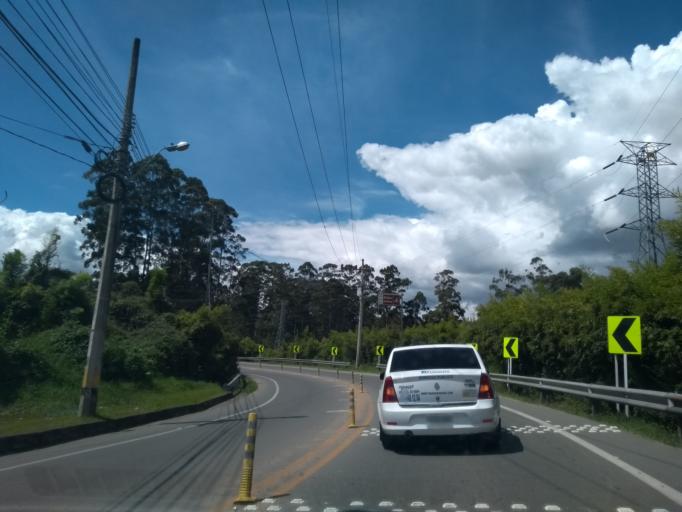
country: CO
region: Antioquia
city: La Ceja
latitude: 6.0426
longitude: -75.4061
